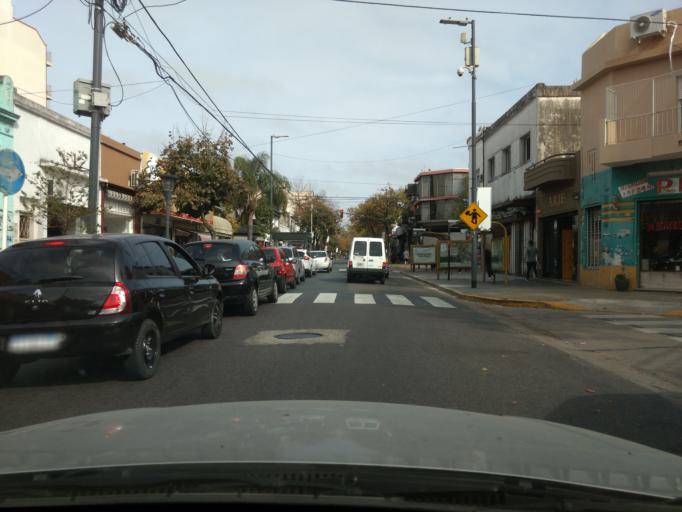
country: AR
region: Buenos Aires F.D.
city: Villa Santa Rita
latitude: -34.6190
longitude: -58.5042
